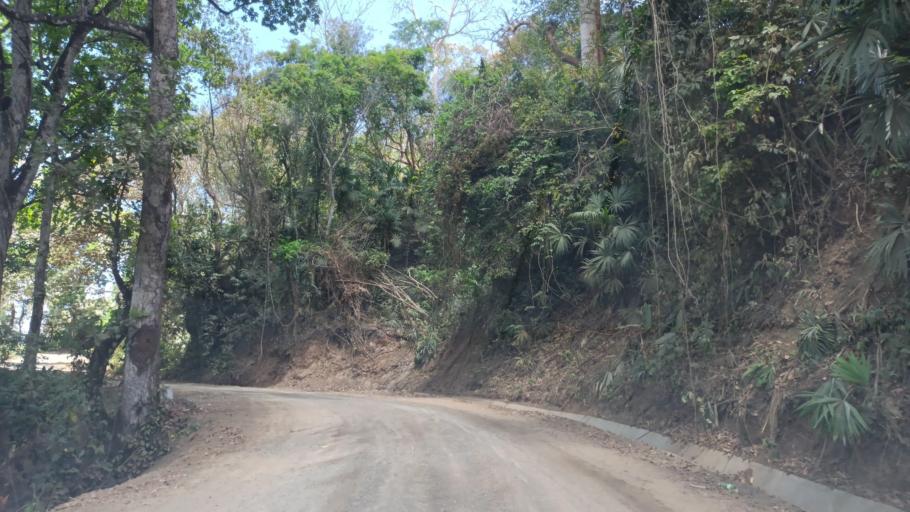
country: PA
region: Panama
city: Las Cumbres
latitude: 9.0745
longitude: -79.5739
